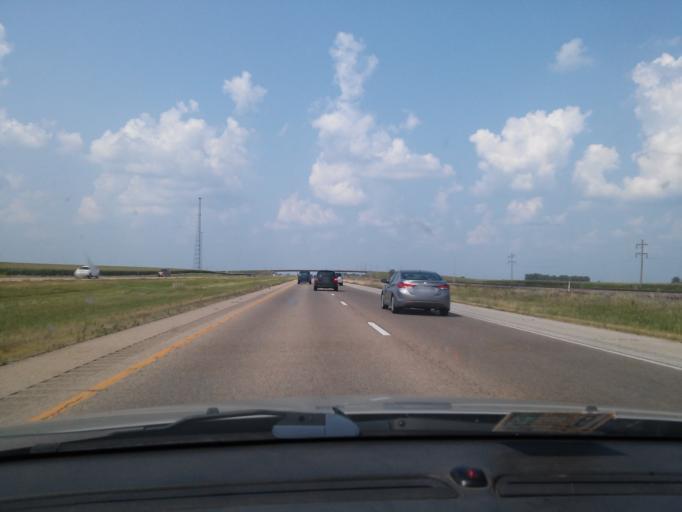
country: US
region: Illinois
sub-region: McLean County
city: Lexington
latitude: 40.6756
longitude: -88.7646
